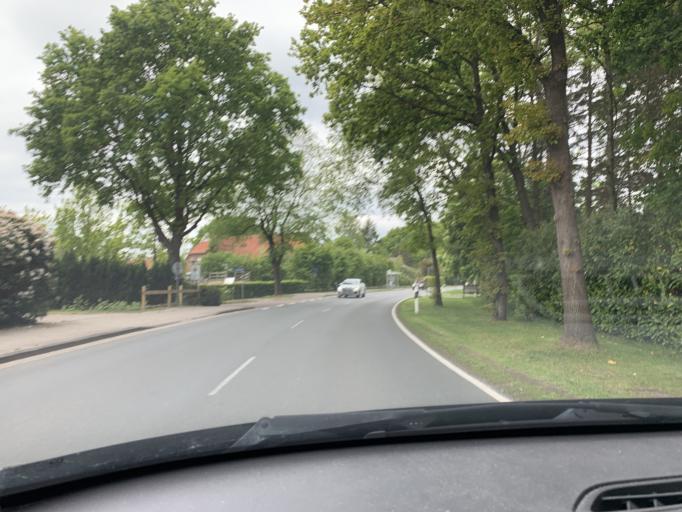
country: DE
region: Lower Saxony
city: Bad Zwischenahn
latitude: 53.1947
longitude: 8.0476
